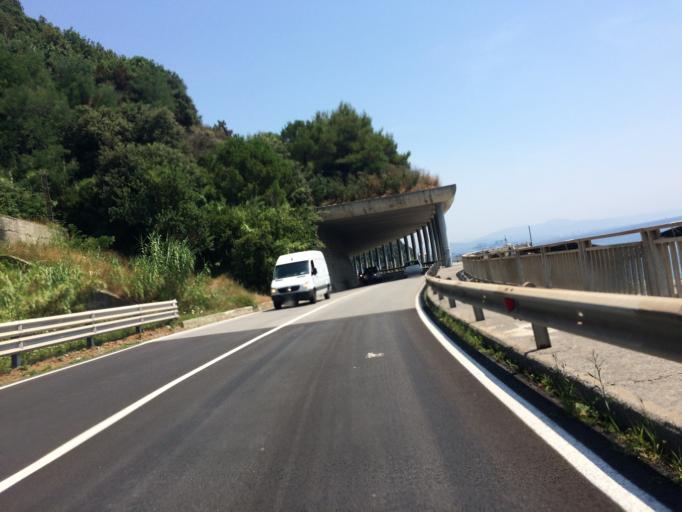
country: IT
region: Liguria
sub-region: Provincia di Genova
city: Arenzano
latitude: 44.4150
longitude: 8.7102
